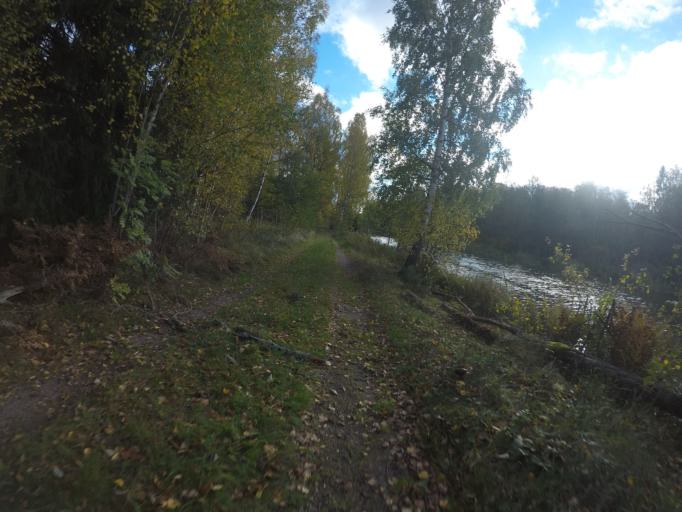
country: SE
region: Vaestmanland
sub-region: Arboga Kommun
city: Tyringe
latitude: 59.3590
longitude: 15.9563
